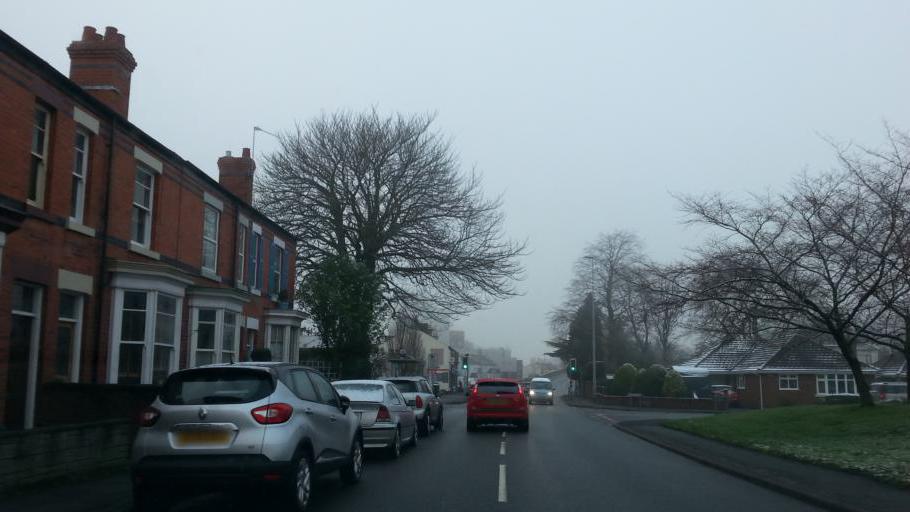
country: GB
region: England
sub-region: Cheshire East
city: Congleton
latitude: 53.1562
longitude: -2.1901
